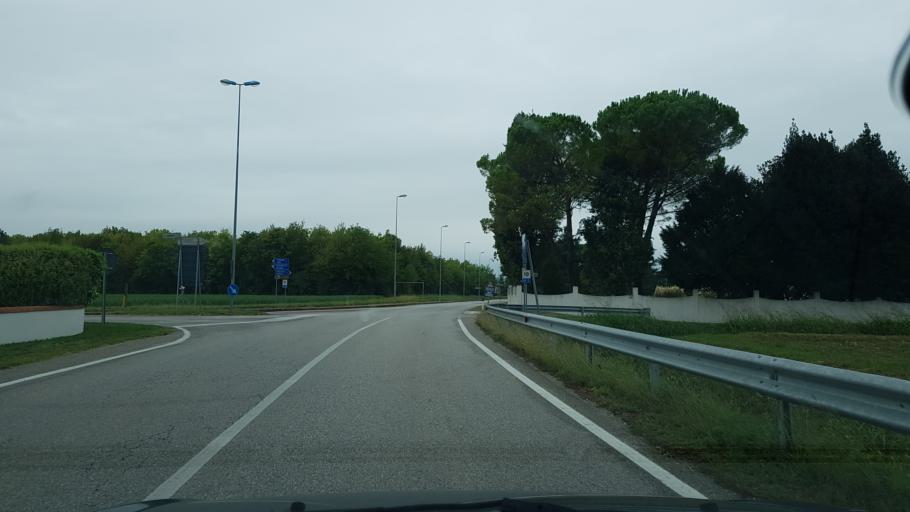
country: IT
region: Friuli Venezia Giulia
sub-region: Provincia di Udine
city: Trivignano Udinese
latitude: 45.9492
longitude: 13.3428
